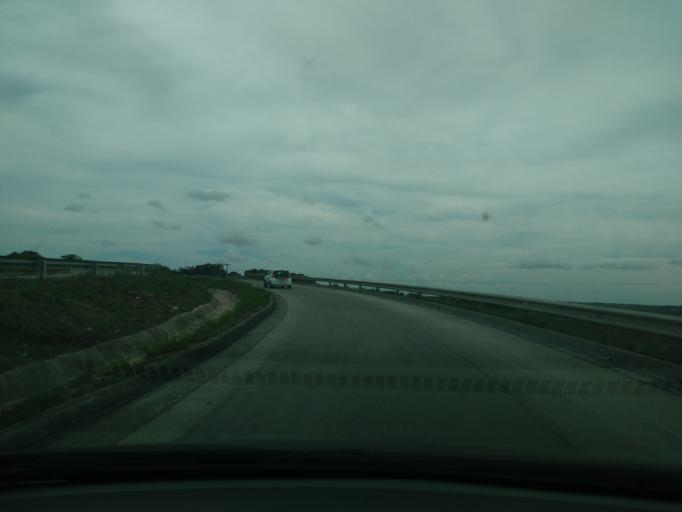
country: BR
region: Alagoas
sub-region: Rio Largo
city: Rio Largo
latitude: -9.4401
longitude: -35.8380
